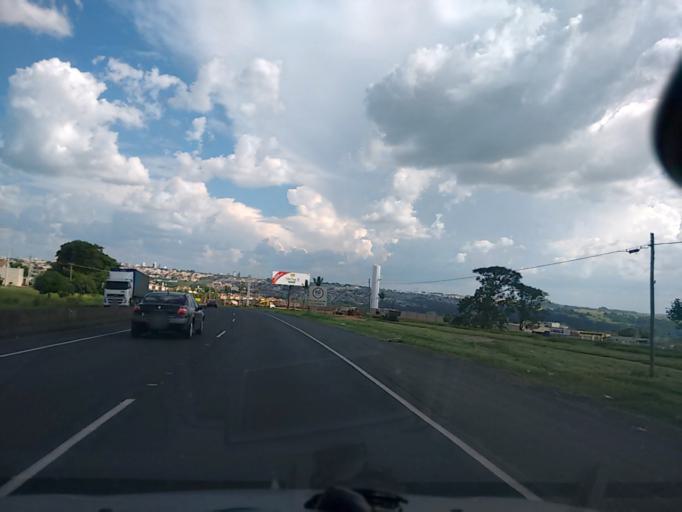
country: BR
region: Sao Paulo
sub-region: Marilia
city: Marilia
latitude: -22.1825
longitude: -49.9723
